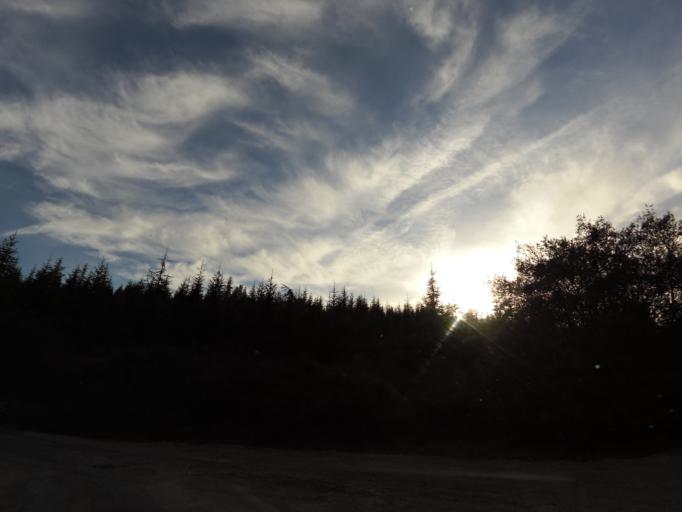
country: FR
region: Languedoc-Roussillon
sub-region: Departement du Gard
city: Congenies
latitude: 43.7878
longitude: 4.1663
